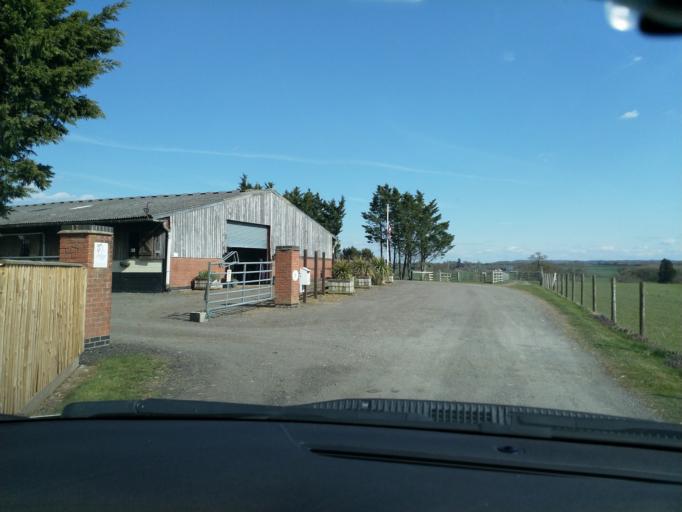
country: GB
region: England
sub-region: Warwickshire
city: Wellesbourne Mountford
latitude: 52.1765
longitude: -1.5489
